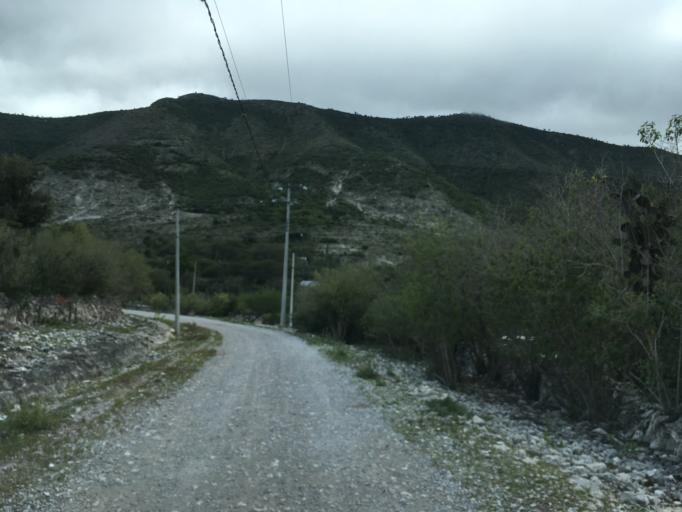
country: MX
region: Hidalgo
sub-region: Metztitlan
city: Fontezuelas
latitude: 20.6258
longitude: -98.8602
